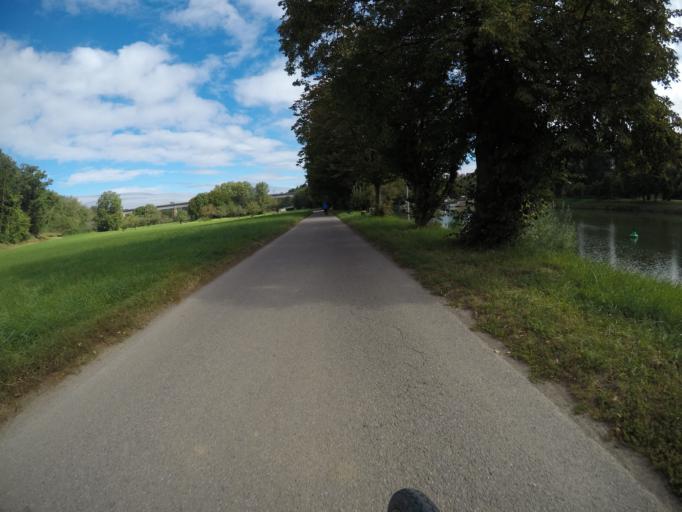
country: DE
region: Baden-Wuerttemberg
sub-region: Regierungsbezirk Stuttgart
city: Marbach am Neckar
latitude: 48.9391
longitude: 9.2506
